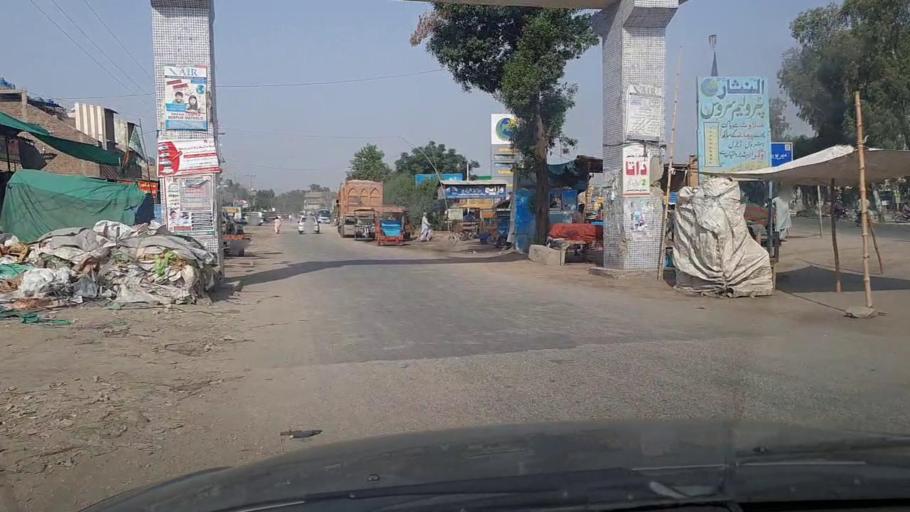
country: PK
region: Sindh
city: Mirpur Mathelo
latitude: 28.0259
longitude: 69.5707
